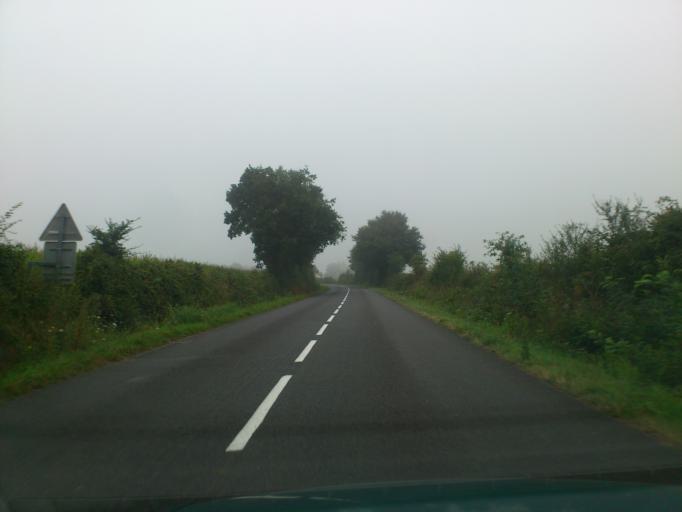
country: FR
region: Pays de la Loire
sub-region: Departement de la Loire-Atlantique
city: Saint-Hilaire-de-Clisson
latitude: 47.0543
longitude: -1.3162
